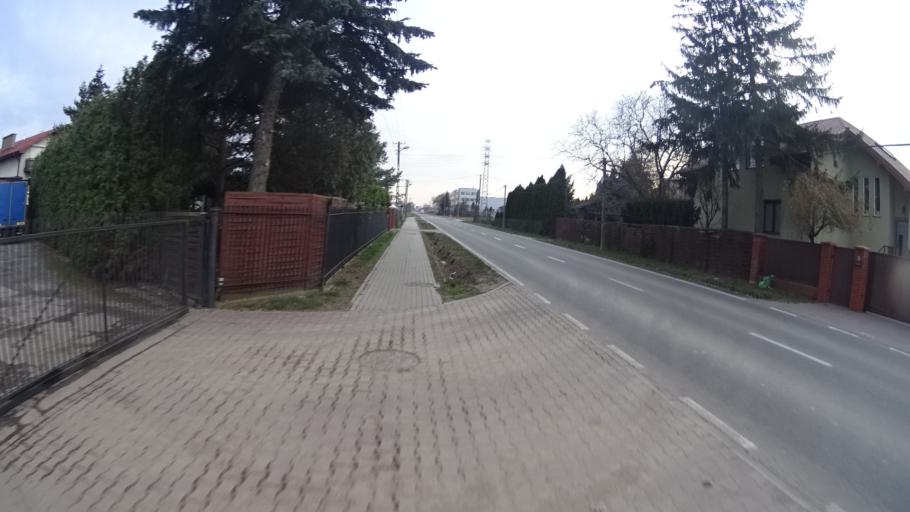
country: PL
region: Masovian Voivodeship
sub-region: Powiat warszawski zachodni
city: Babice
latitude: 52.2219
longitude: 20.8601
